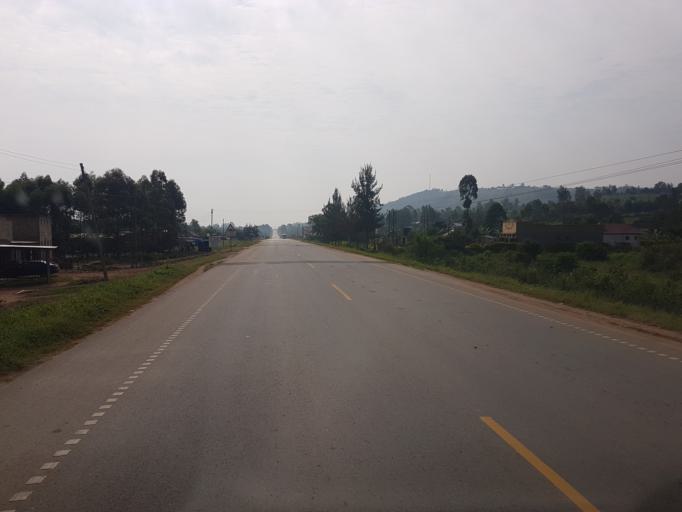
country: UG
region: Western Region
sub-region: Sheema District
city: Kibingo
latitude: -0.6435
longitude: 30.4995
